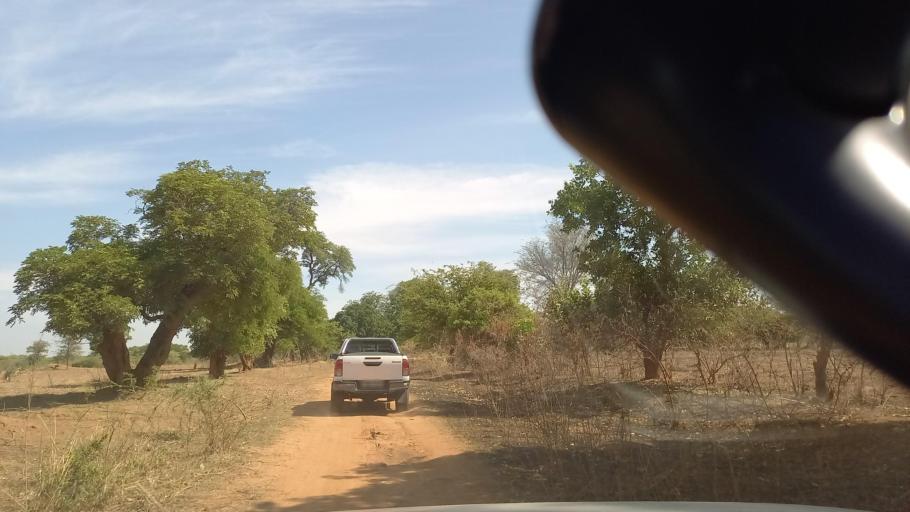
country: ZM
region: Southern
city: Mazabuka
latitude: -16.0343
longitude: 27.6232
